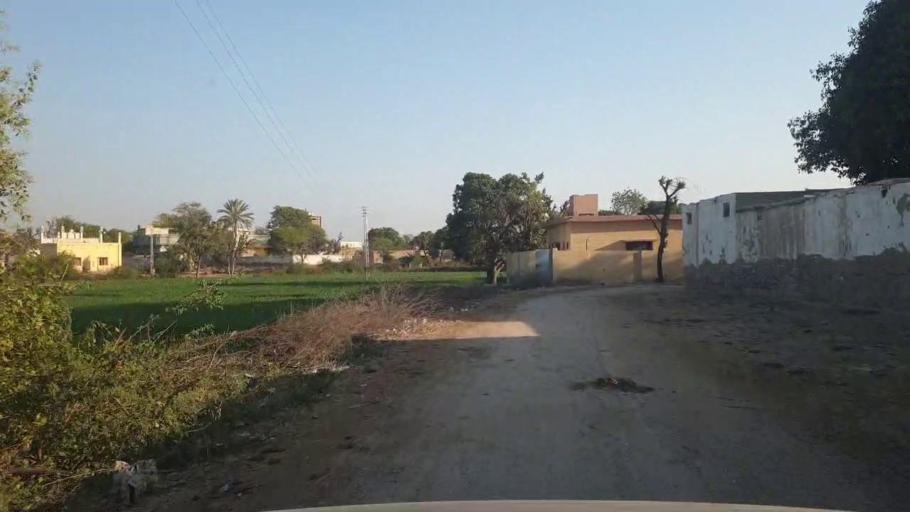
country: PK
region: Sindh
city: Chambar
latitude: 25.2577
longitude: 68.8956
